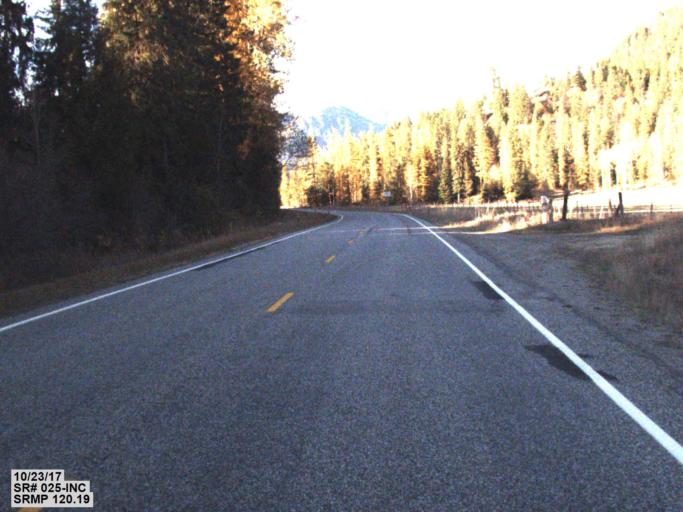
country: CA
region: British Columbia
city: Rossland
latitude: 48.9861
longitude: -117.8272
